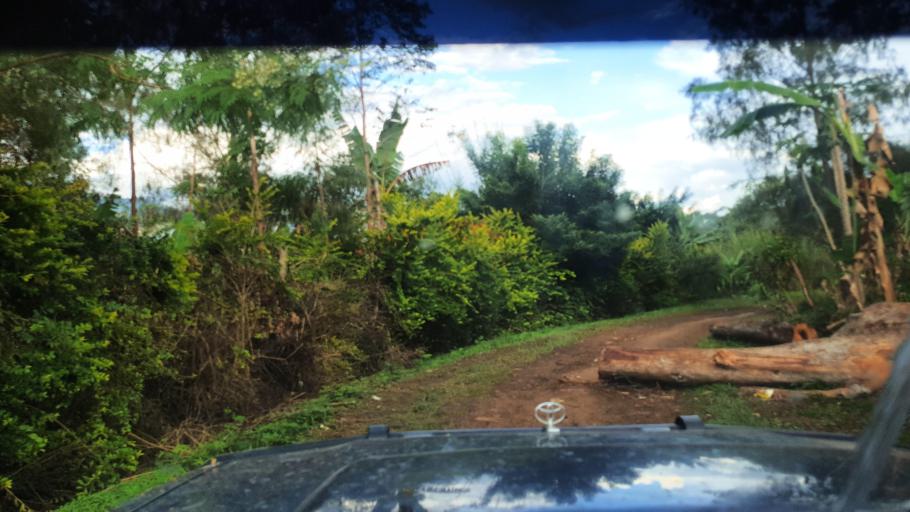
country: PG
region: Jiwaka
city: Minj
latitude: -5.9397
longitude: 144.8195
